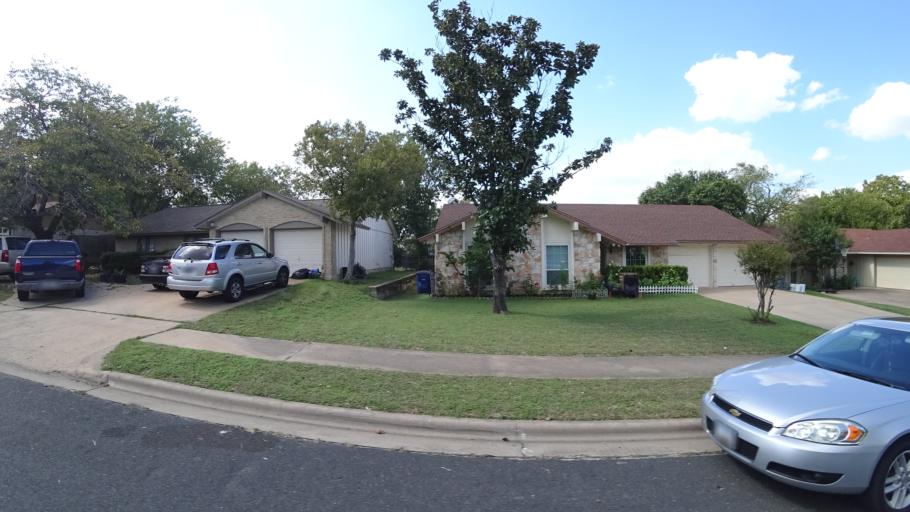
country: US
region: Texas
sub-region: Travis County
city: Wells Branch
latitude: 30.3650
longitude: -97.7122
